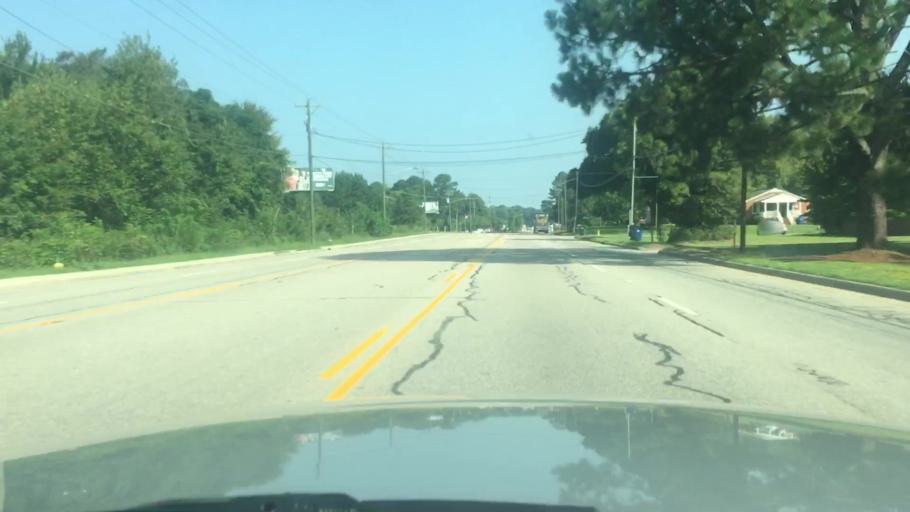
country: US
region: North Carolina
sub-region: Cumberland County
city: Vander
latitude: 35.0223
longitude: -78.8410
